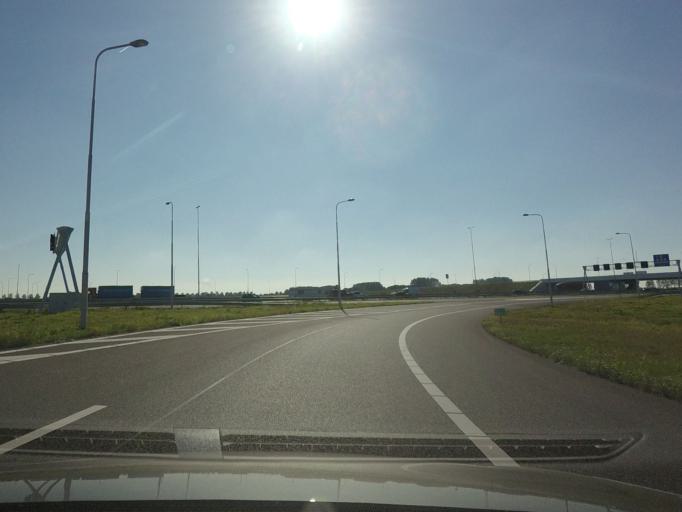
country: NL
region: North Holland
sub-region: Gemeente Haarlemmermeer
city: Hoofddorp
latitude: 52.2741
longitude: 4.7048
